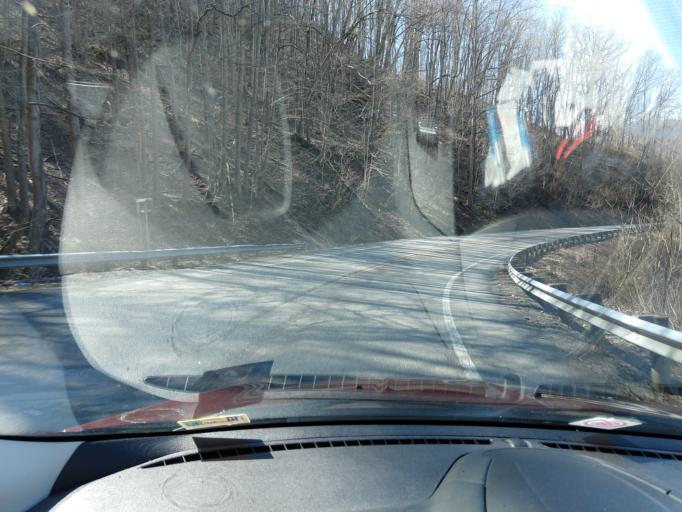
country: US
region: West Virginia
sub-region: Summers County
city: Hinton
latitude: 37.7495
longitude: -80.9073
